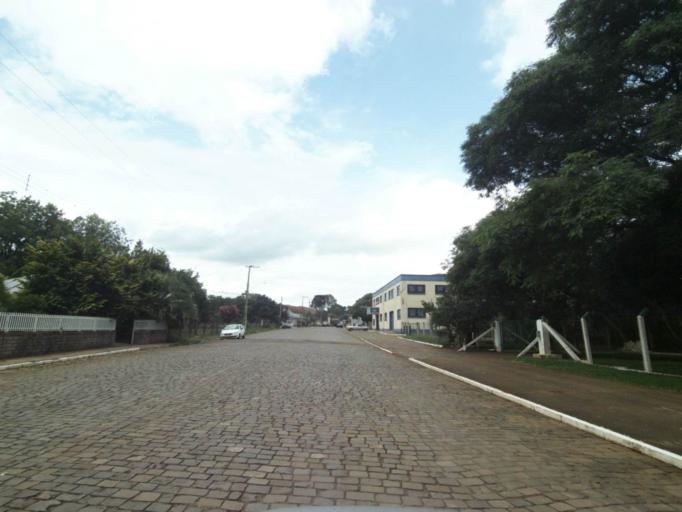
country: BR
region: Rio Grande do Sul
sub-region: Lagoa Vermelha
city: Lagoa Vermelha
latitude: -28.2086
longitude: -51.5412
